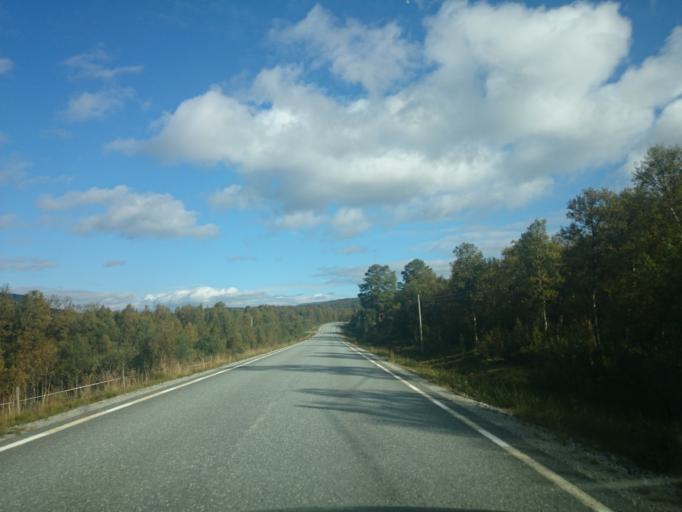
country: NO
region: Sor-Trondelag
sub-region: Tydal
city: Aas
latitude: 62.6531
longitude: 12.4259
